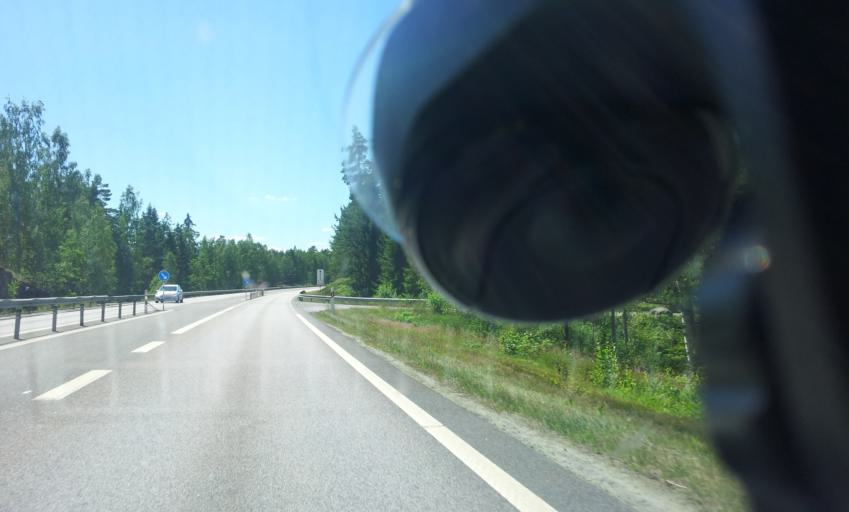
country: SE
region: OEstergoetland
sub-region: Valdemarsviks Kommun
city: Valdemarsvik
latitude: 58.1005
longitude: 16.5374
